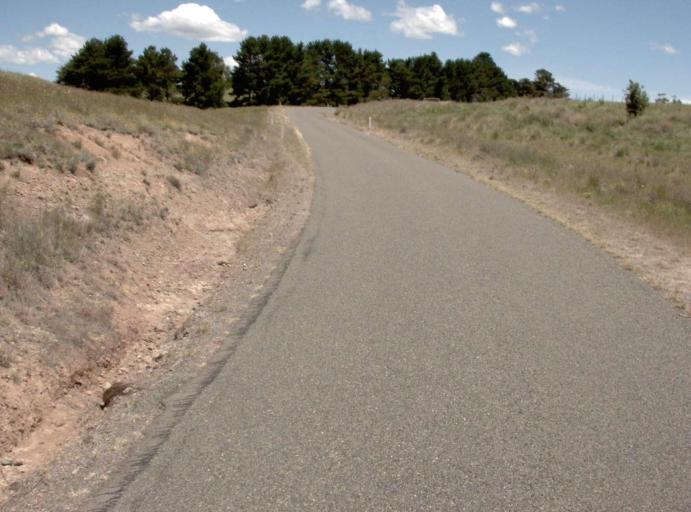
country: AU
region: New South Wales
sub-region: Snowy River
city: Jindabyne
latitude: -37.0795
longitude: 148.2810
